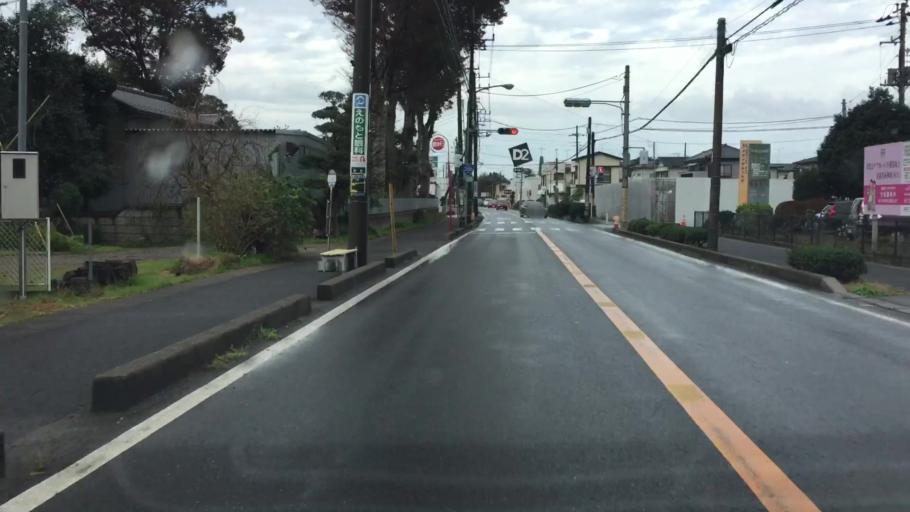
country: JP
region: Ibaraki
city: Toride
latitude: 35.8627
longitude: 140.1153
